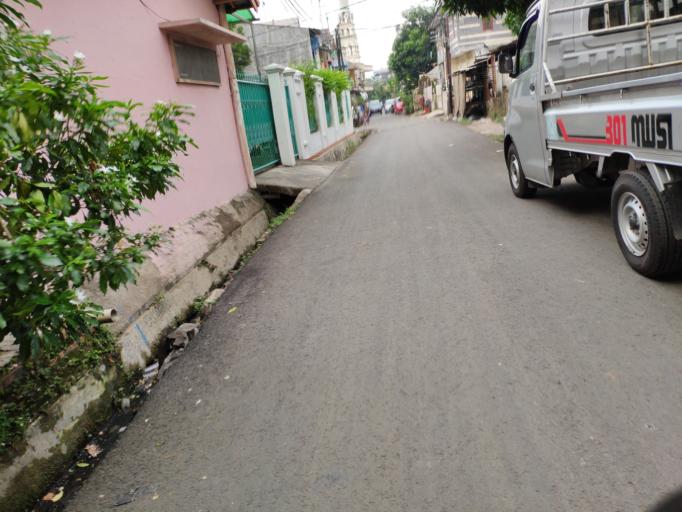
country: ID
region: Jakarta Raya
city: Jakarta
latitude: -6.2007
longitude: 106.8672
